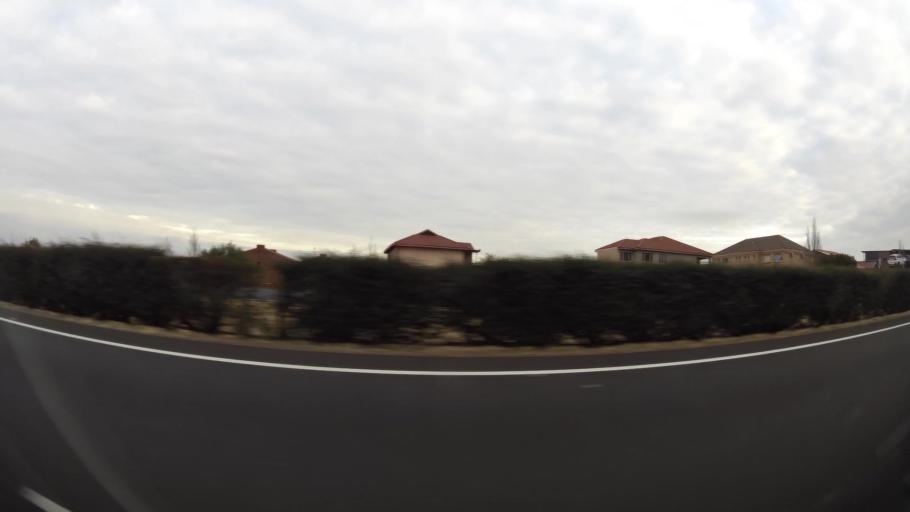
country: ZA
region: Orange Free State
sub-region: Mangaung Metropolitan Municipality
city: Bloemfontein
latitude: -29.1000
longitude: 26.1654
